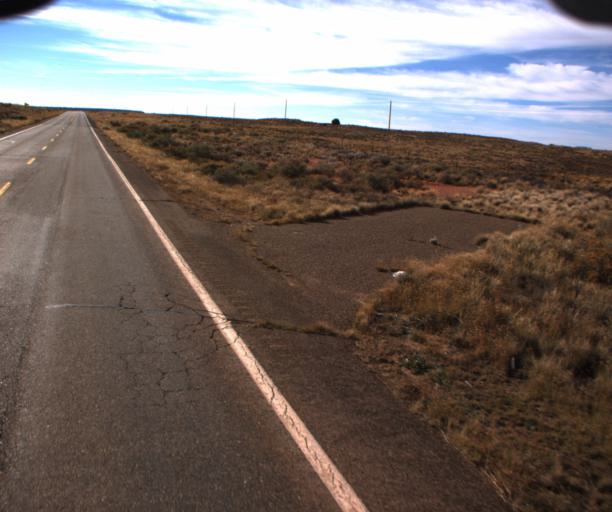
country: US
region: Arizona
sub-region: Coconino County
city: LeChee
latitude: 36.7192
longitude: -111.2761
